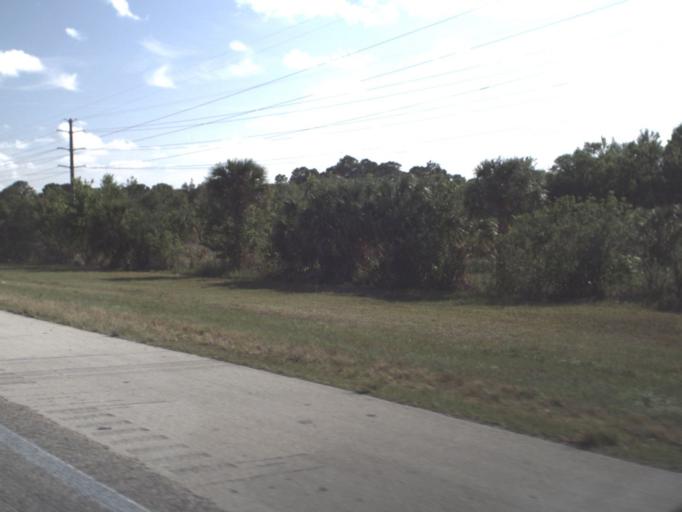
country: US
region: Florida
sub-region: Brevard County
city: June Park
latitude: 28.1283
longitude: -80.7061
